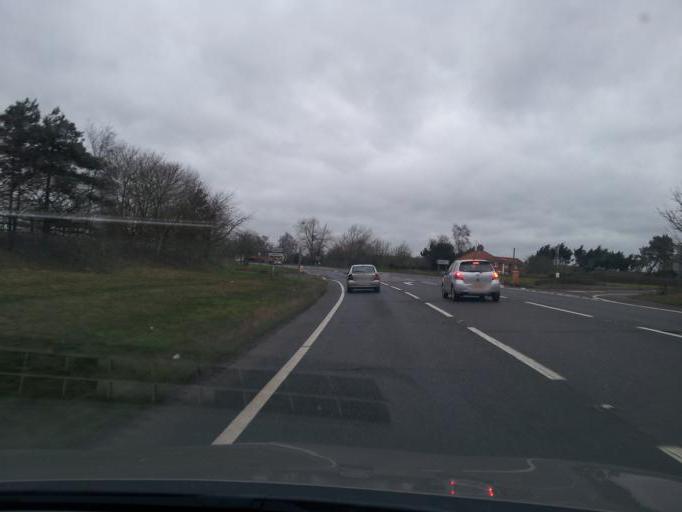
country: GB
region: England
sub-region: Suffolk
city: Ixworth
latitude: 52.2927
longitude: 0.8306
